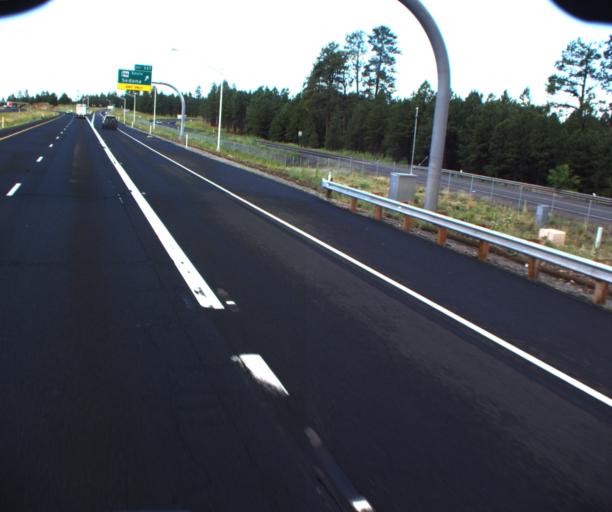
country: US
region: Arizona
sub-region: Coconino County
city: Kachina Village
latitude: 35.1462
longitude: -111.6833
